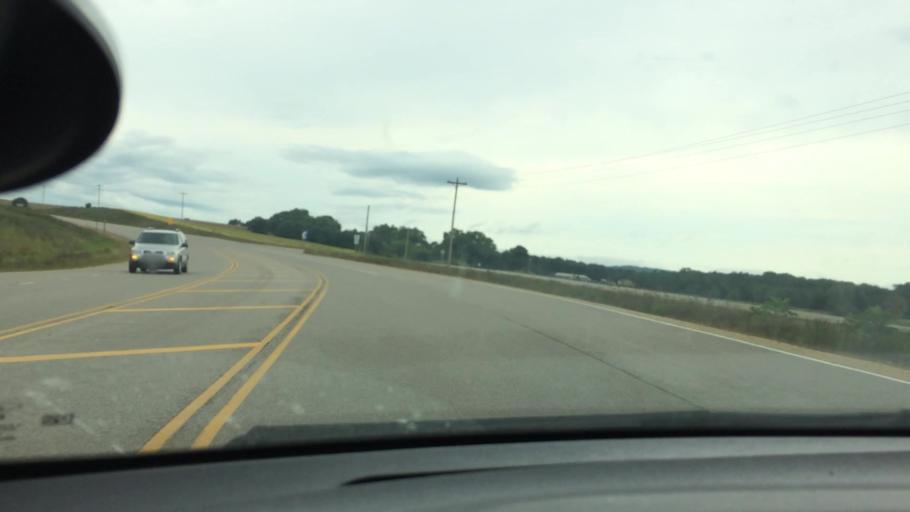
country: US
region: Wisconsin
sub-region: Trempealeau County
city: Osseo
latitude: 44.5903
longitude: -91.1757
